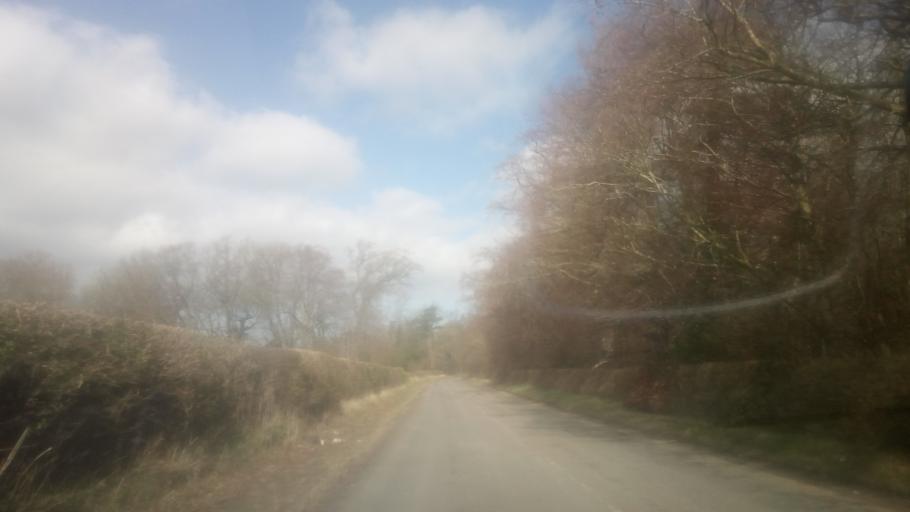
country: GB
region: Scotland
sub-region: Fife
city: Pathhead
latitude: 55.8842
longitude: -2.9596
